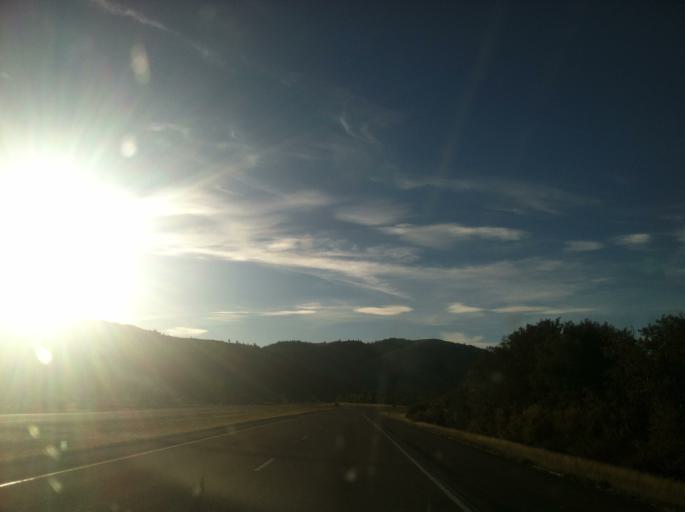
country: US
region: Montana
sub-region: Granite County
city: Philipsburg
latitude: 46.6804
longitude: -113.1864
